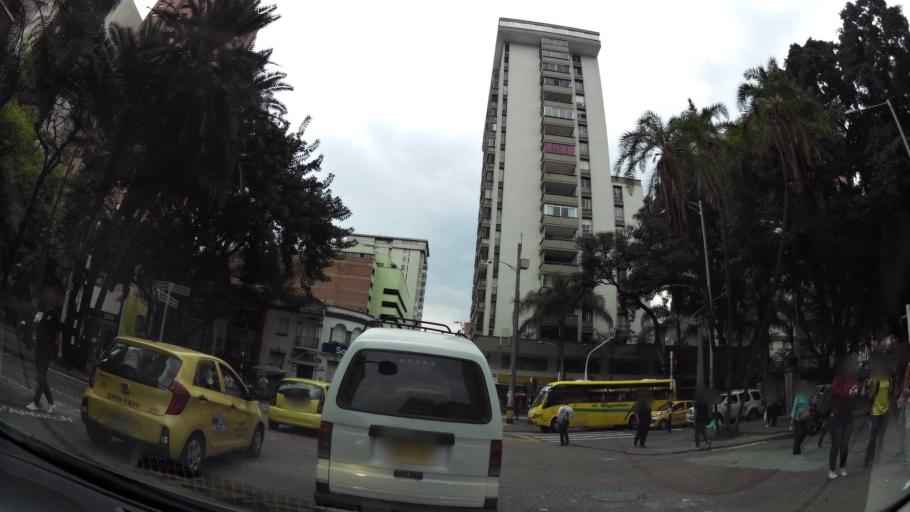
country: CO
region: Antioquia
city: Medellin
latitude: 6.2486
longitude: -75.5637
